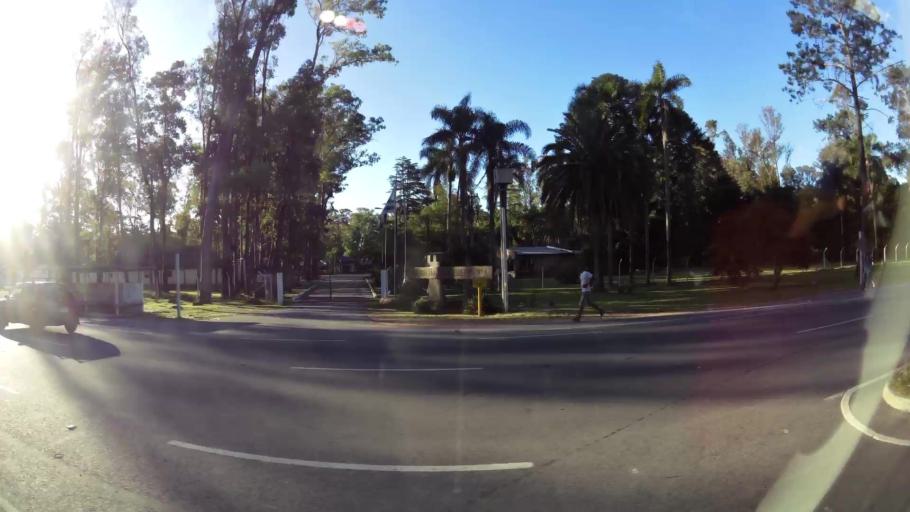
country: UY
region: Canelones
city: Paso de Carrasco
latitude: -34.8507
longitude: -56.0359
